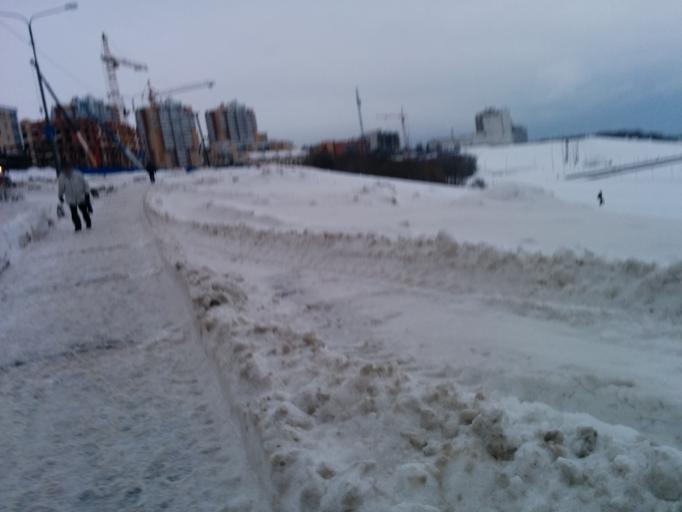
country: RU
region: Chuvashia
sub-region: Cheboksarskiy Rayon
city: Cheboksary
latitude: 56.1390
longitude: 47.2321
